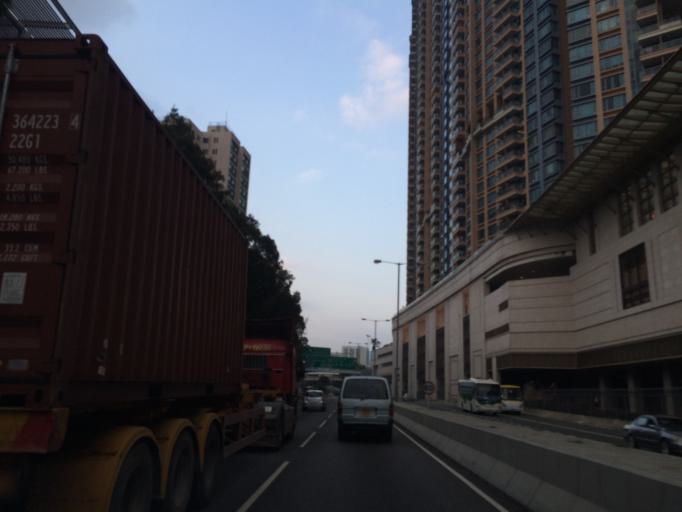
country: HK
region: Sha Tin
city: Sha Tin
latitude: 22.3959
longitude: 114.2002
